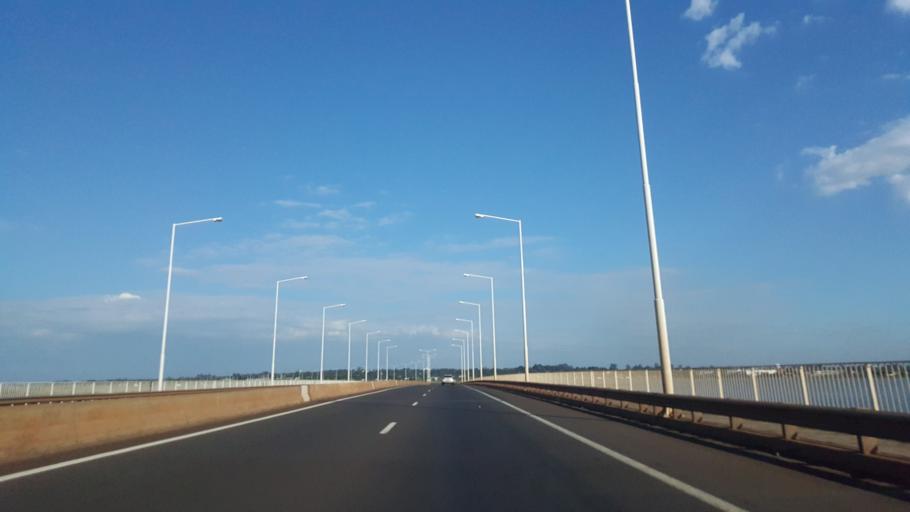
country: AR
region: Misiones
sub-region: Departamento de Capital
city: Posadas
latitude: -27.4054
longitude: -55.8919
